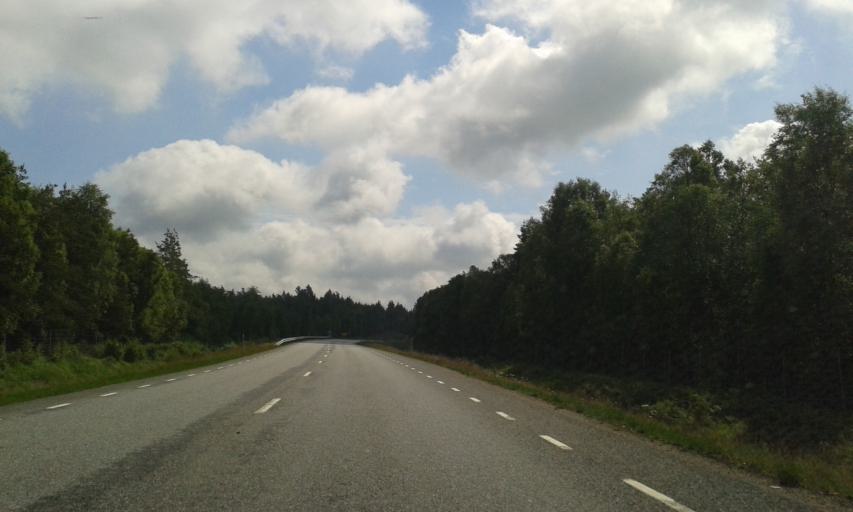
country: SE
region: Vaestra Goetaland
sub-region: Tranemo Kommun
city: Langhem
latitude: 57.5679
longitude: 13.2494
